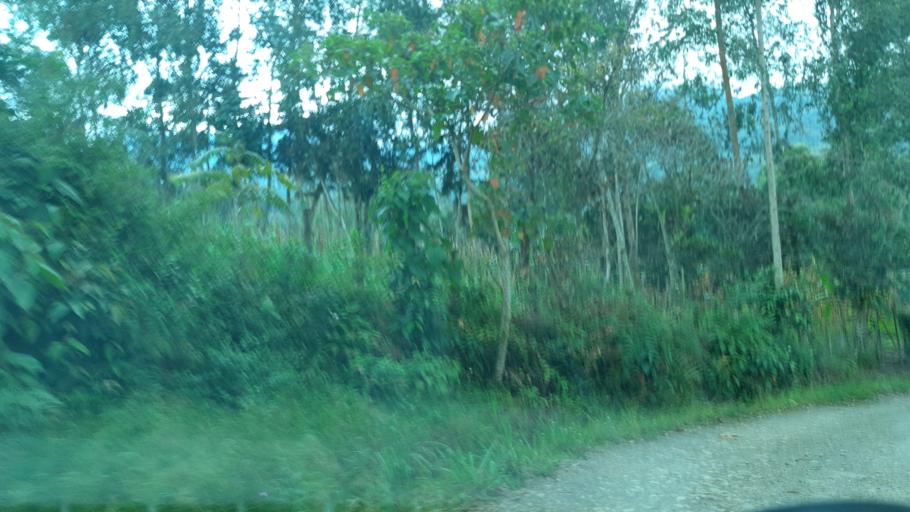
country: CO
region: Boyaca
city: Chinavita
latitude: 5.1372
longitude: -73.3433
